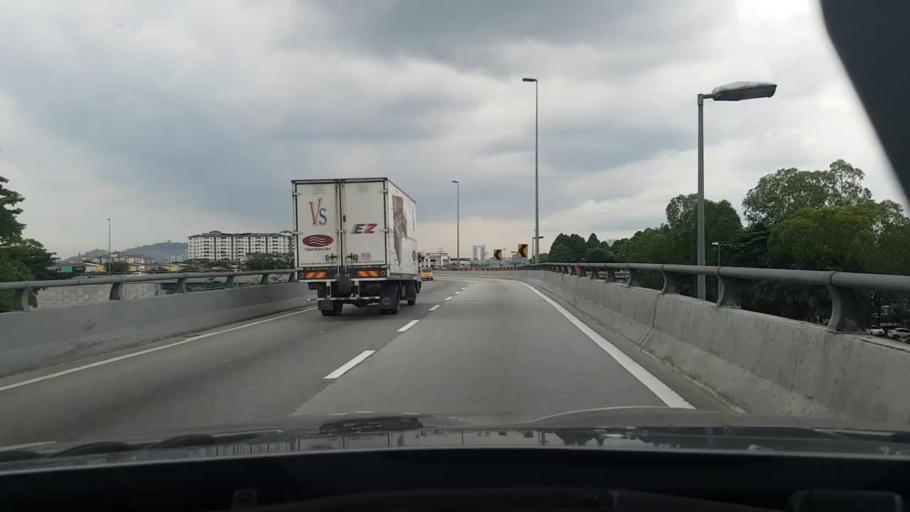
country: MY
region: Selangor
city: Subang Jaya
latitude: 3.0202
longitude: 101.6116
